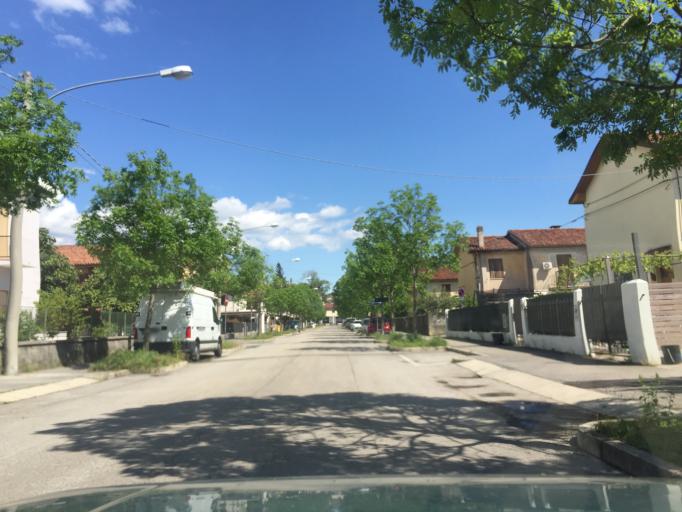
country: IT
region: Friuli Venezia Giulia
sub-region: Provincia di Gorizia
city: Gorizia
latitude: 45.9297
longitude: 13.6024
